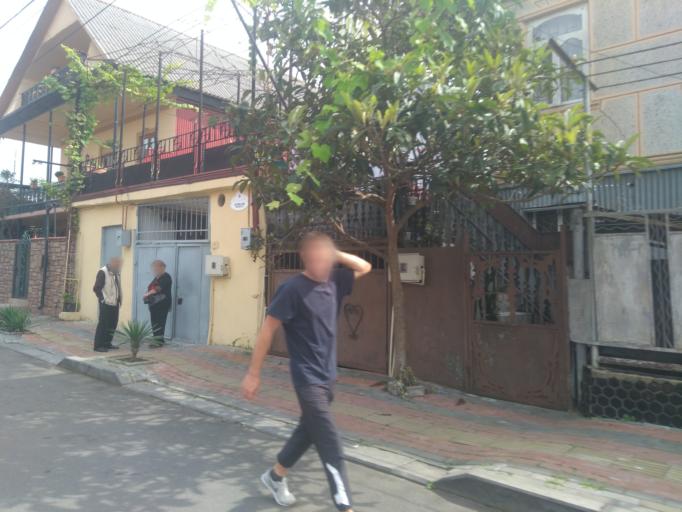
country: GE
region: Ajaria
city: Batumi
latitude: 41.6415
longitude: 41.6498
